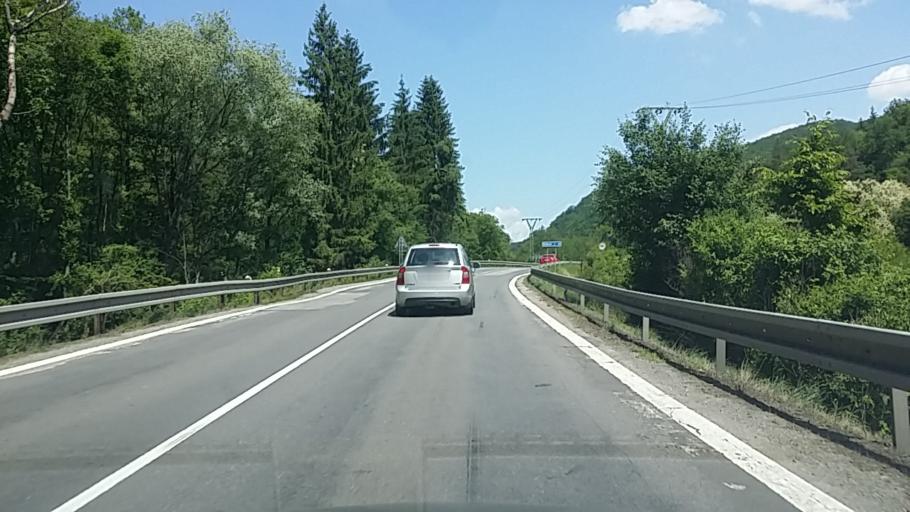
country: SK
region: Banskobystricky
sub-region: Okres Banska Bystrica
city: Zvolen
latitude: 48.5329
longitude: 19.1164
